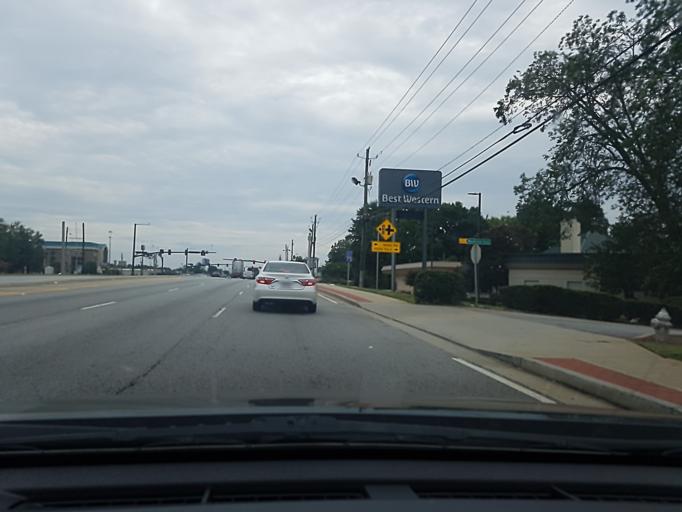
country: US
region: Georgia
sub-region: Clayton County
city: Morrow
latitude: 33.5801
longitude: -84.3404
